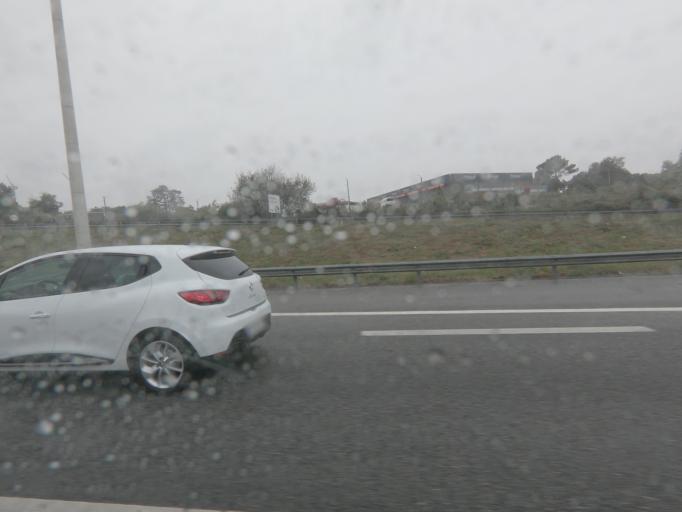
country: PT
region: Porto
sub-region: Maia
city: Pedroucos
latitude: 41.1830
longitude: -8.5934
